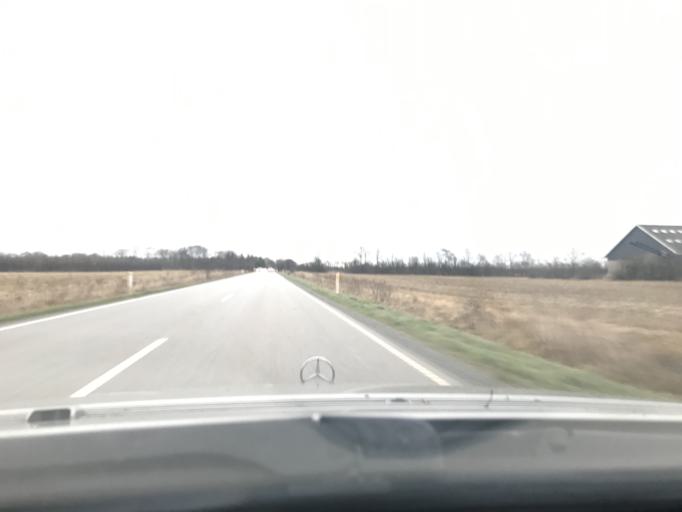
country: DK
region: South Denmark
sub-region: Aabenraa Kommune
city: Rodekro
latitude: 55.0745
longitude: 9.2988
